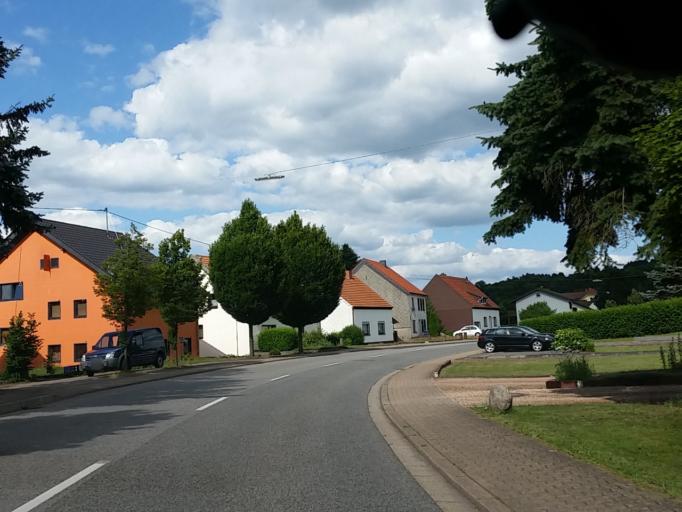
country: DE
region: Saarland
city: Wadern
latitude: 49.5286
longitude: 6.9669
